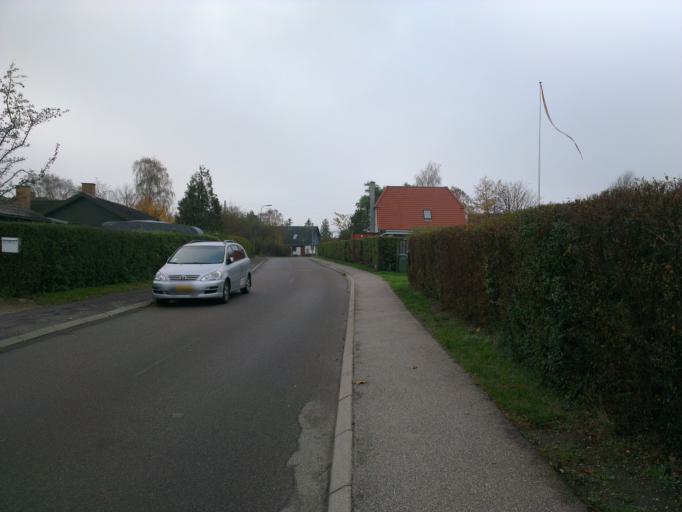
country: DK
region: Capital Region
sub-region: Frederikssund Kommune
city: Jaegerspris
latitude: 55.8540
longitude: 11.9977
